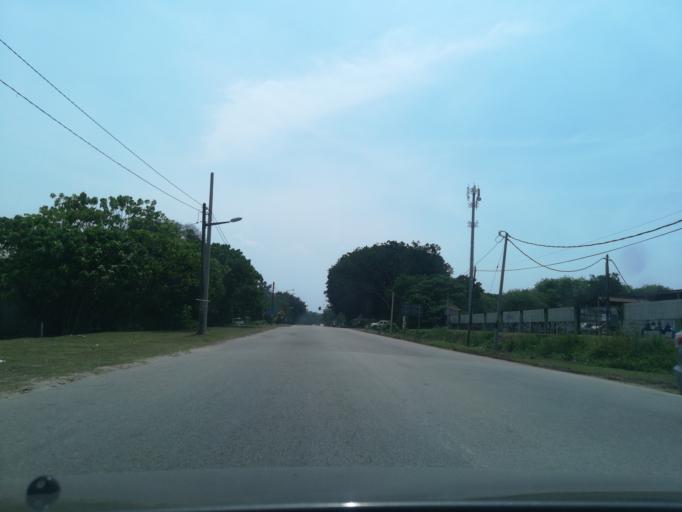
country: MY
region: Kedah
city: Kulim
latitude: 5.4125
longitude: 100.5634
